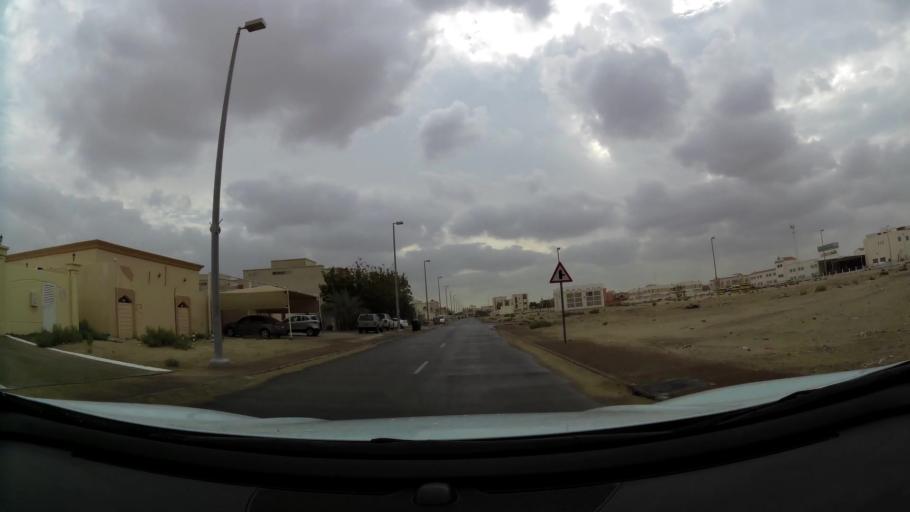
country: AE
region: Abu Dhabi
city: Abu Dhabi
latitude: 24.3544
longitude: 54.6390
